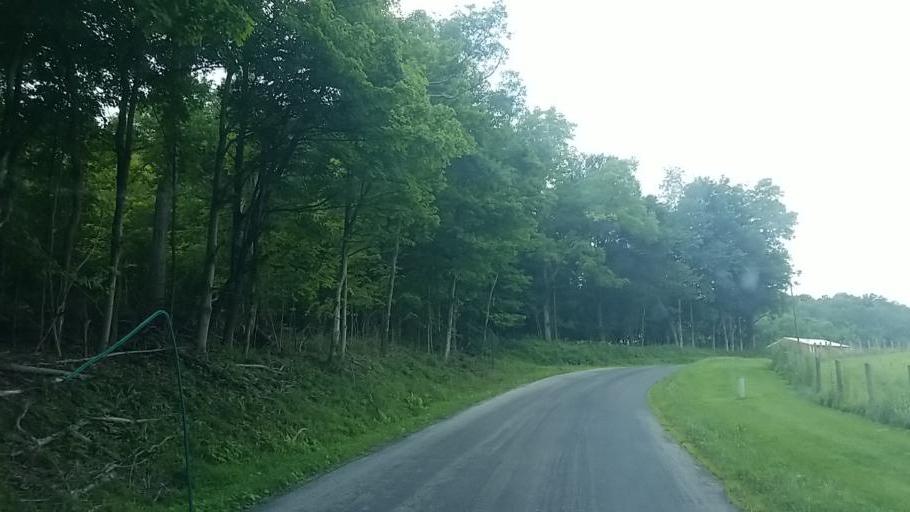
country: US
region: Ohio
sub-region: Muskingum County
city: Frazeysburg
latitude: 40.2203
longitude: -82.2217
